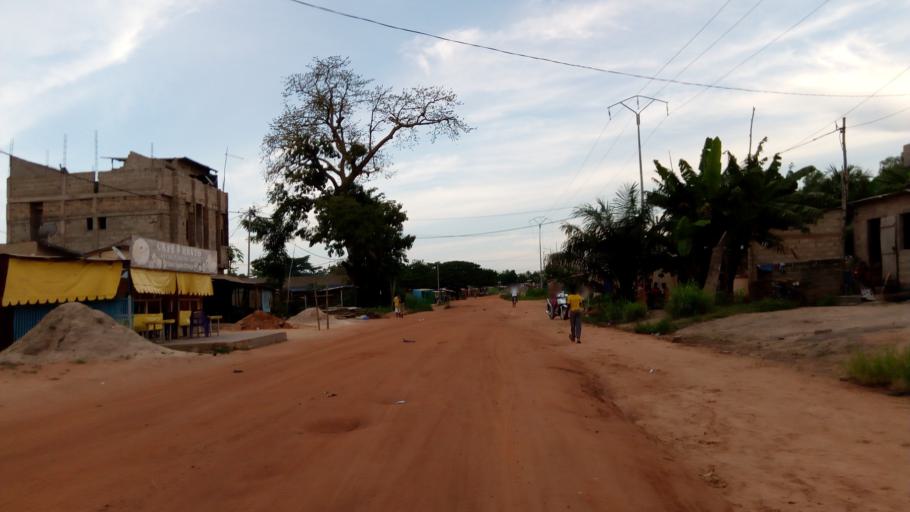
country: TG
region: Maritime
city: Lome
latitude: 6.2507
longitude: 1.1398
